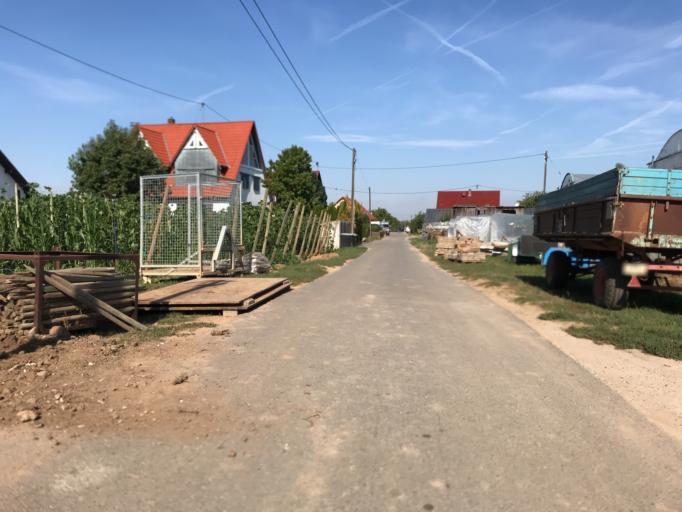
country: DE
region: Baden-Wuerttemberg
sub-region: Karlsruhe Region
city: Dossenheim
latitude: 49.4306
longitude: 8.6737
